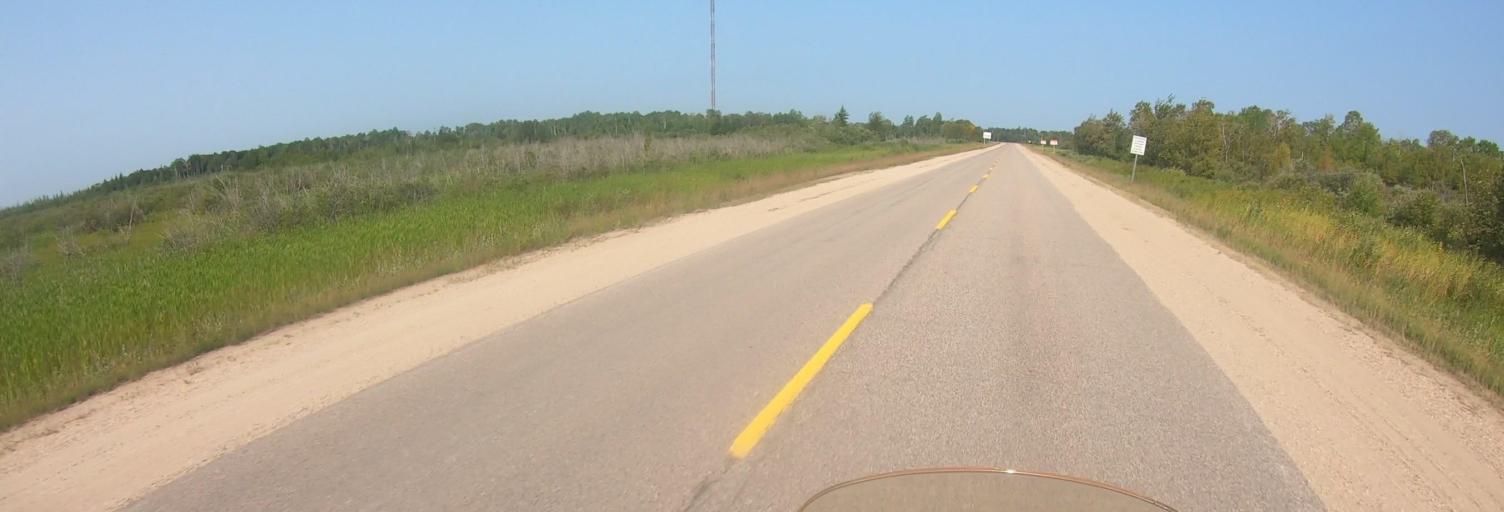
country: US
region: Minnesota
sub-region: Roseau County
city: Warroad
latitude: 49.0132
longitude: -95.4002
